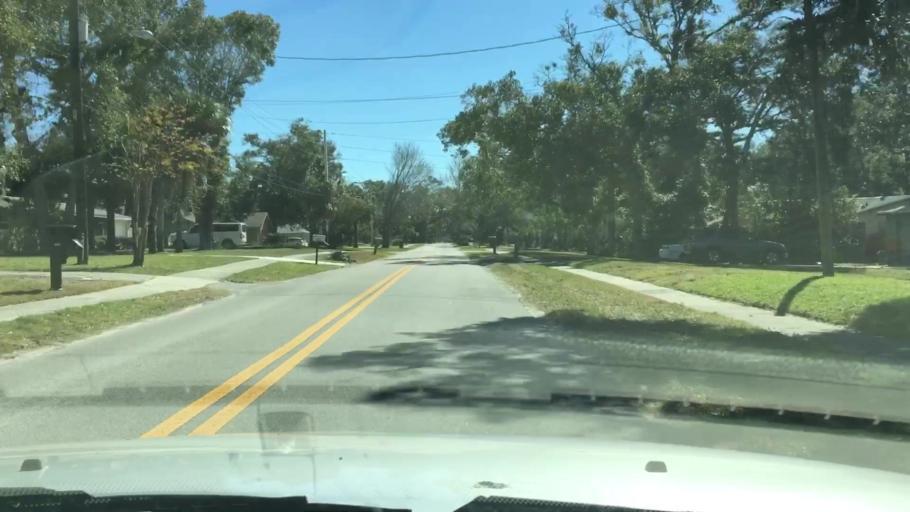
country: US
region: Florida
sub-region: Volusia County
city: Ormond Beach
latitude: 29.3000
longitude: -81.0664
